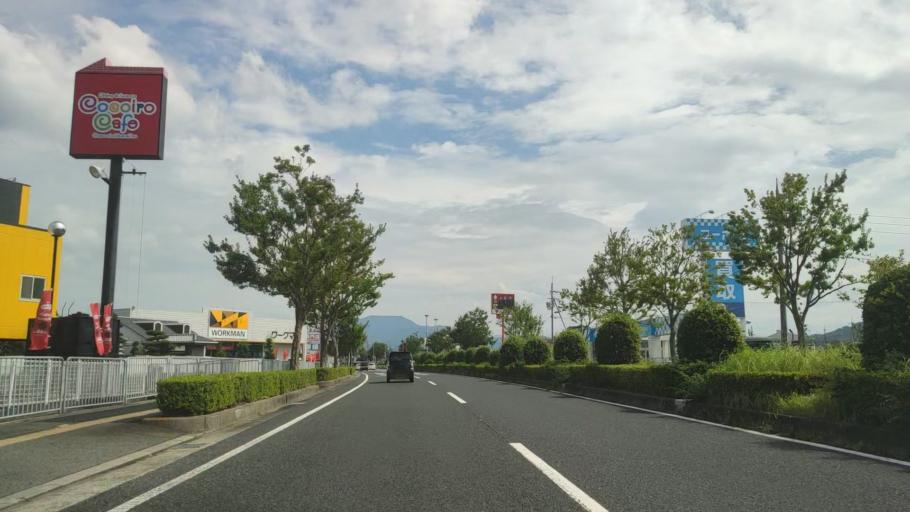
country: JP
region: Wakayama
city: Iwade
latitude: 34.2597
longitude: 135.3003
